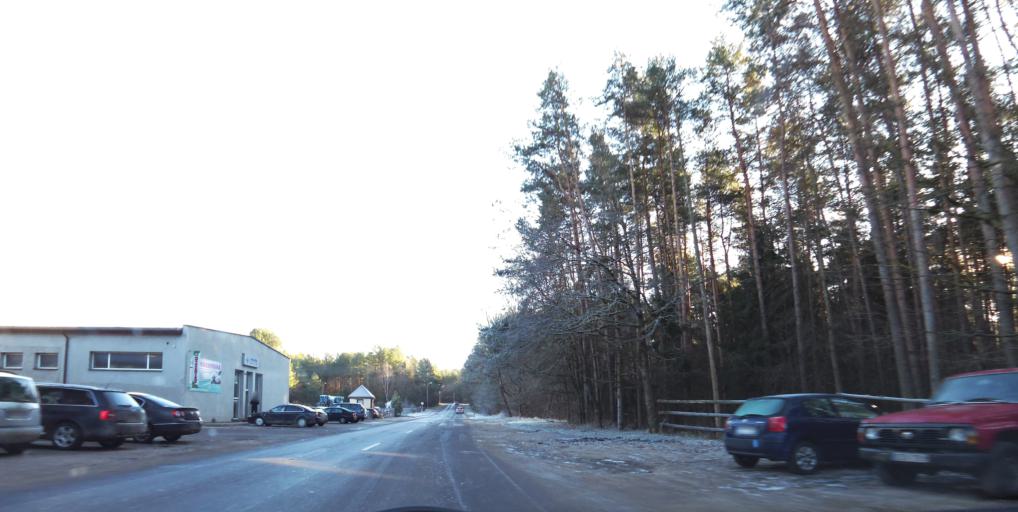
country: LT
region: Vilnius County
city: Lazdynai
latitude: 54.6417
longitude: 25.1751
